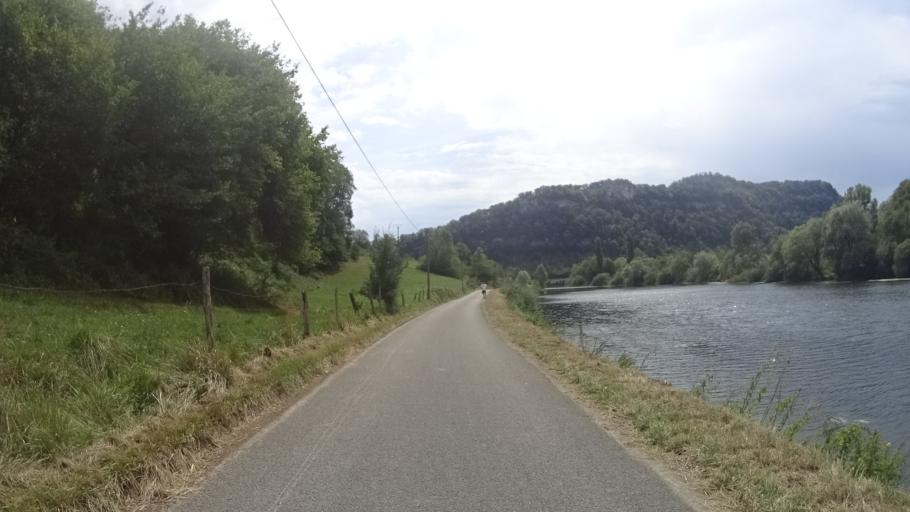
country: FR
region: Franche-Comte
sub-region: Departement du Doubs
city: Baume-les-Dames
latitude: 47.3476
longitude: 6.3742
